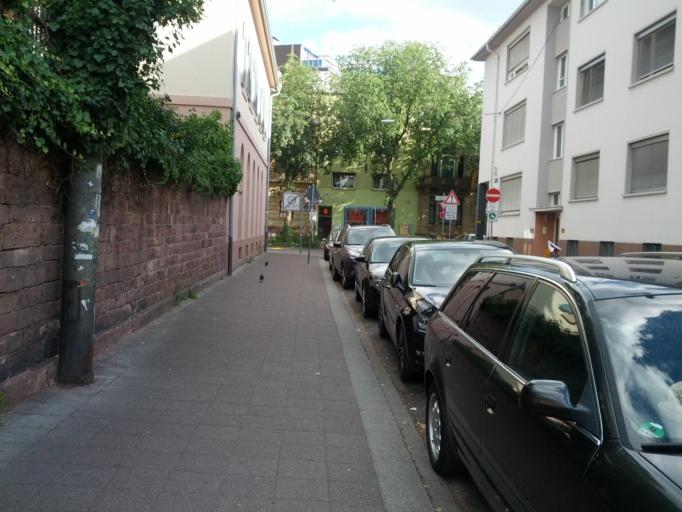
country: DE
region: Baden-Wuerttemberg
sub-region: Karlsruhe Region
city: Karlsruhe
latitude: 49.0122
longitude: 8.3946
